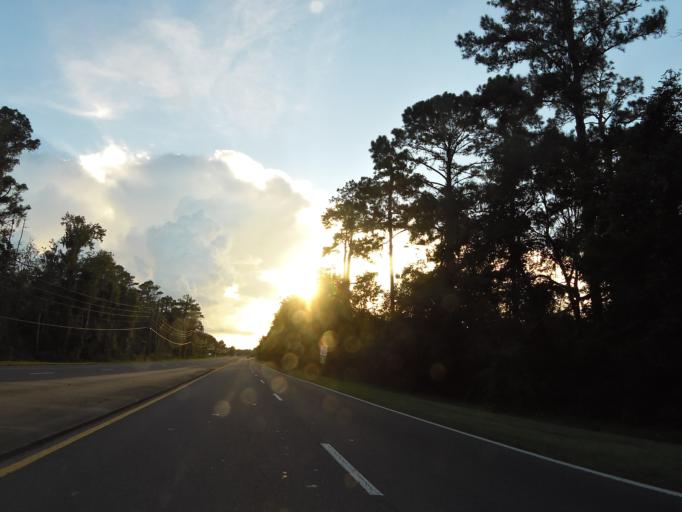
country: US
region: Georgia
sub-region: Camden County
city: Kings Bay Base
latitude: 30.7917
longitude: -81.5779
